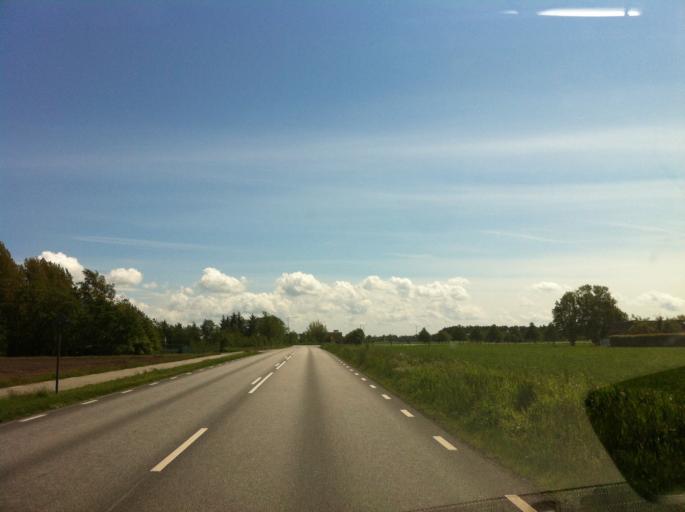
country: SE
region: Skane
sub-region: Kavlinge Kommun
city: Loddekopinge
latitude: 55.7776
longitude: 13.0081
